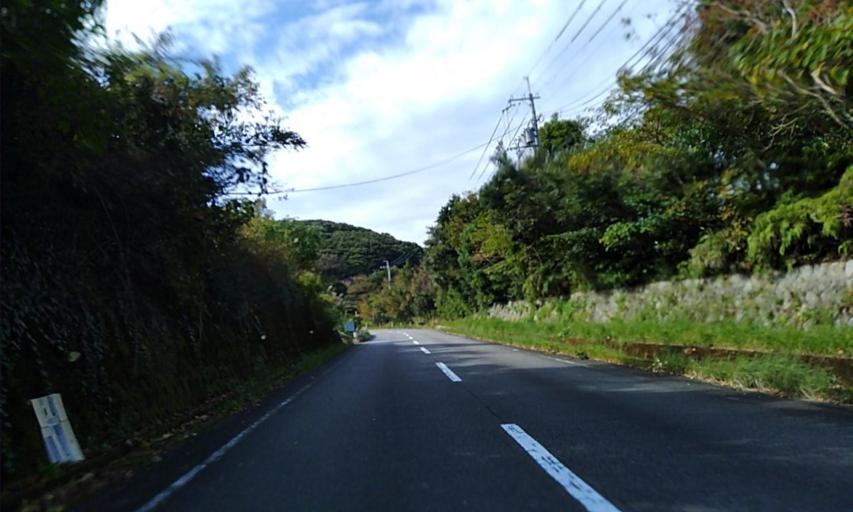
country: JP
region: Wakayama
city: Shingu
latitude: 33.4696
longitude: 135.8368
